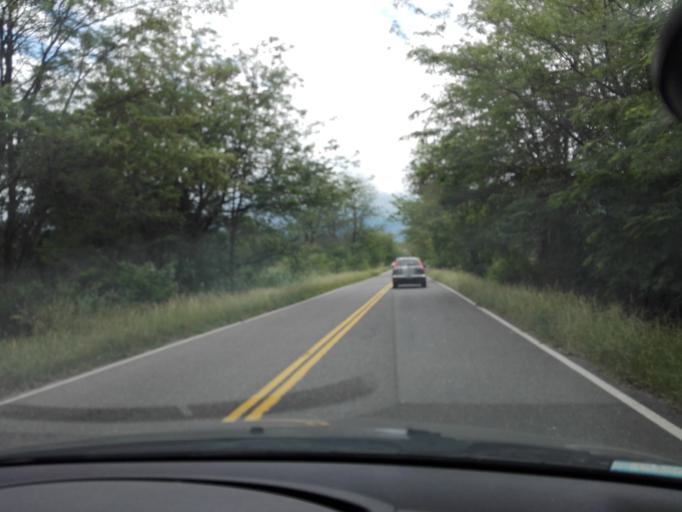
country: AR
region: Cordoba
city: Cuesta Blanca
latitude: -31.6054
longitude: -64.5568
